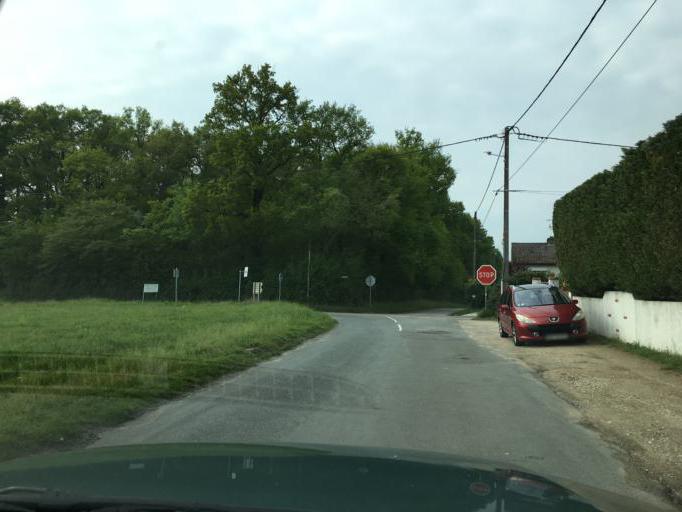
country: FR
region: Centre
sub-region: Departement du Loiret
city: Clery-Saint-Andre
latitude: 47.8138
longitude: 1.7664
